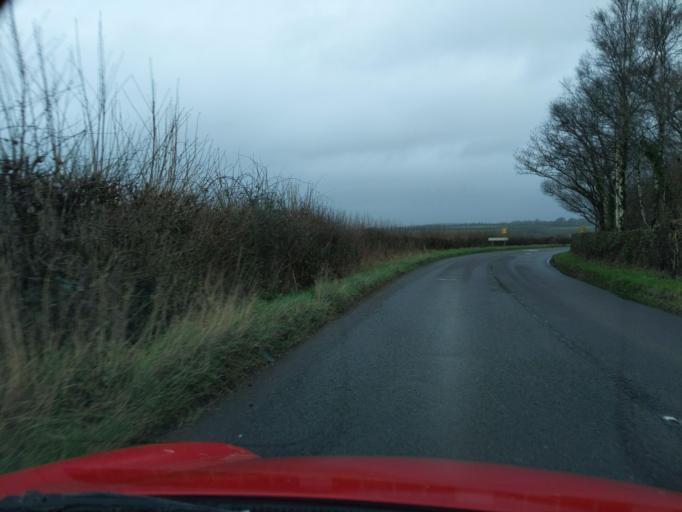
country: GB
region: England
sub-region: Cornwall
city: Werrington
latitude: 50.6821
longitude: -4.3240
